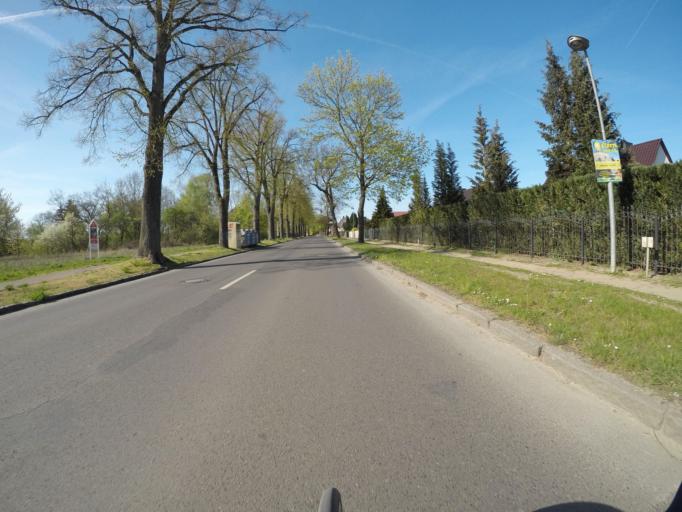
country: DE
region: Brandenburg
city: Rehfelde
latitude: 52.4775
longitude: 13.8527
